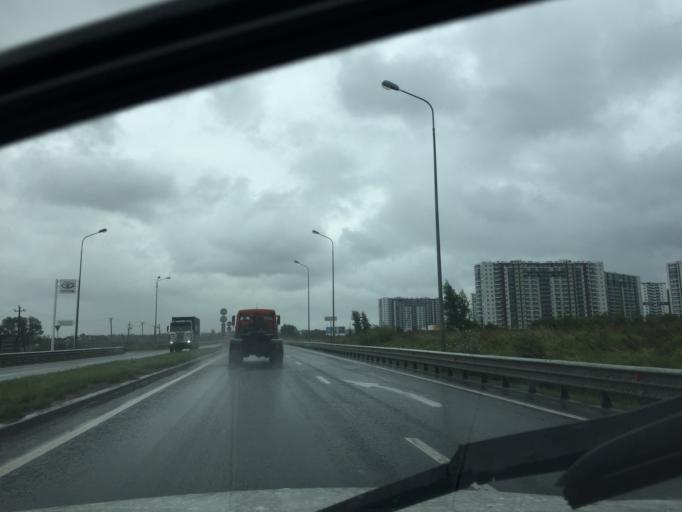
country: RU
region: St.-Petersburg
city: Sosnovaya Polyana
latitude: 59.7967
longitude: 30.1631
